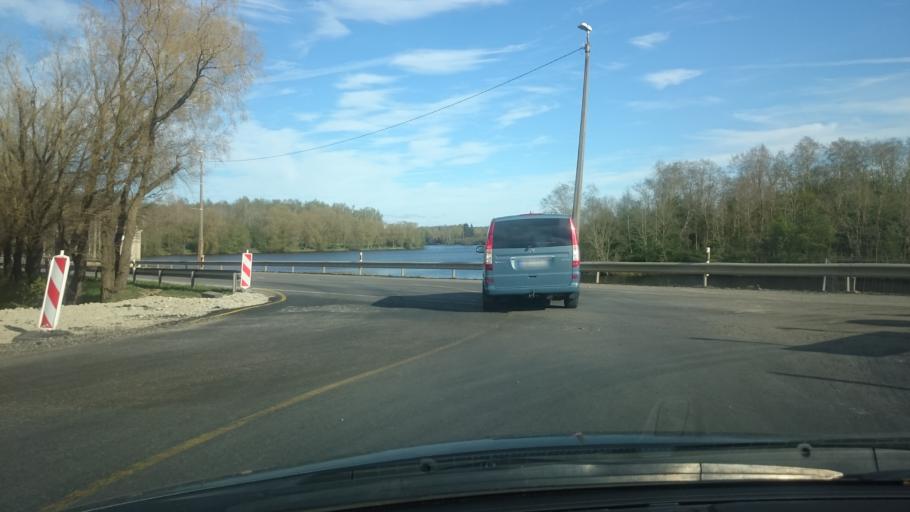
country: EE
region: Ida-Virumaa
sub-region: Sillamaee linn
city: Sillamae
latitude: 59.3913
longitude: 27.7551
